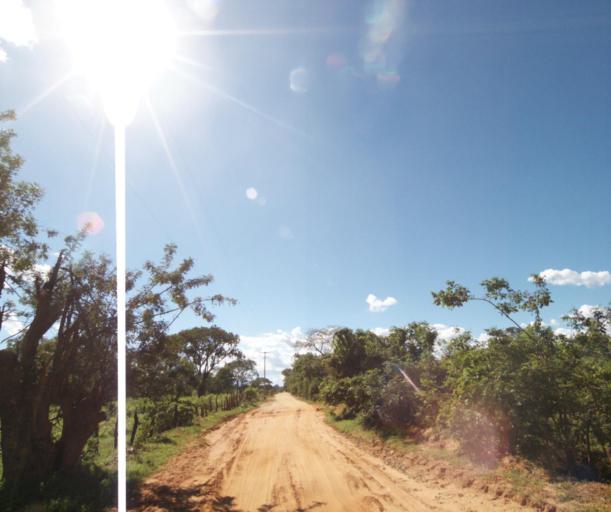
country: BR
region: Bahia
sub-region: Carinhanha
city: Carinhanha
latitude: -14.1848
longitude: -44.5000
